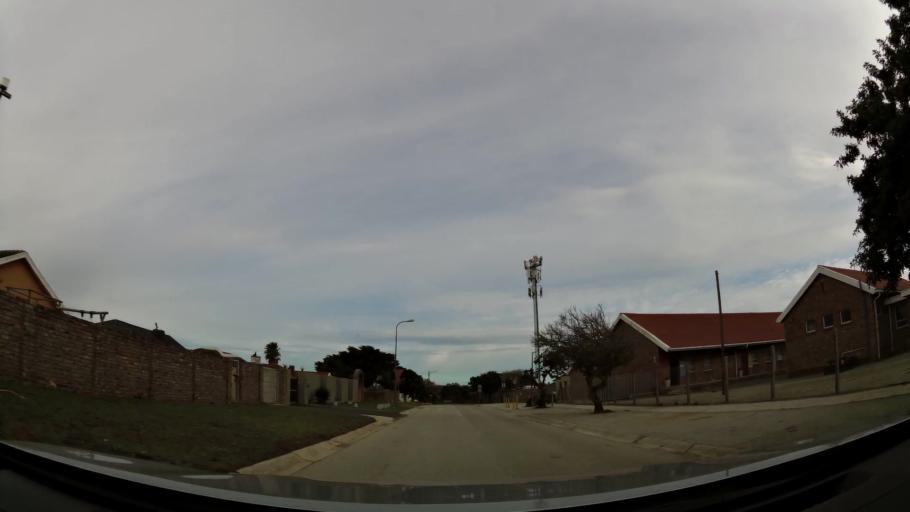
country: ZA
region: Eastern Cape
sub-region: Nelson Mandela Bay Metropolitan Municipality
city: Port Elizabeth
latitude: -33.9439
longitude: 25.4945
